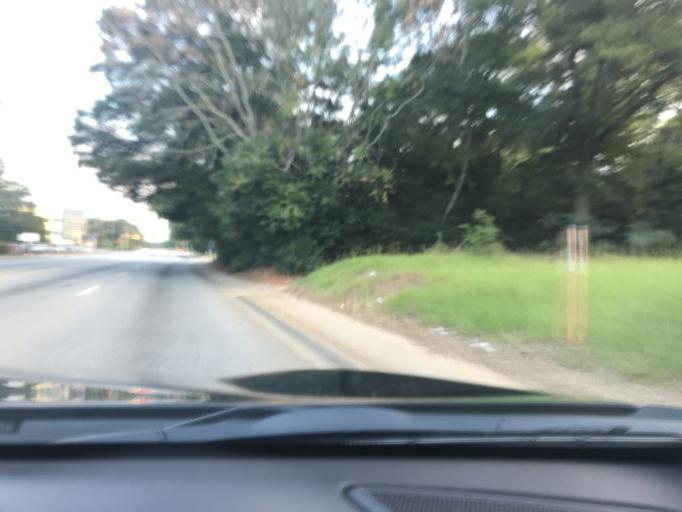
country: US
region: South Carolina
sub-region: Greenville County
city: Welcome
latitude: 34.8220
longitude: -82.4303
